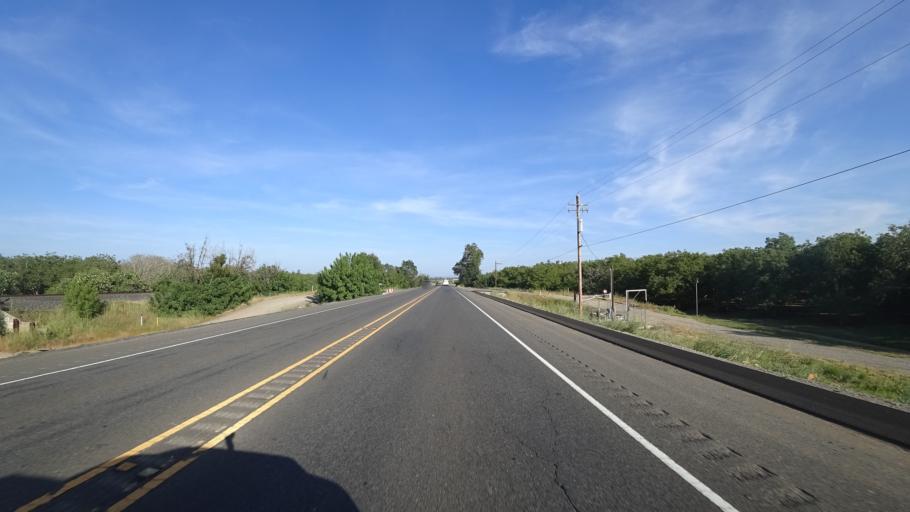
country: US
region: California
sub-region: Yuba County
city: Wheatland
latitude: 38.9987
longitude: -121.4045
